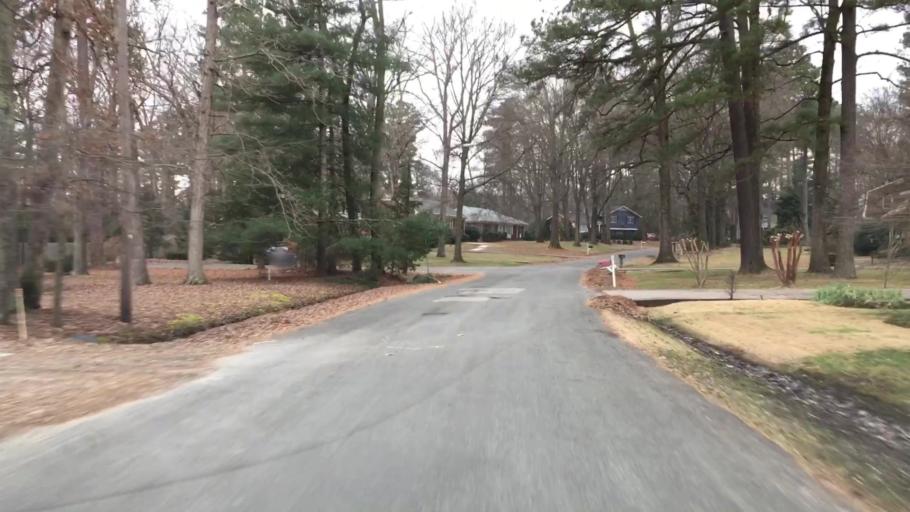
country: US
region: Virginia
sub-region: Chesterfield County
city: Bon Air
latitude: 37.5338
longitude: -77.5775
